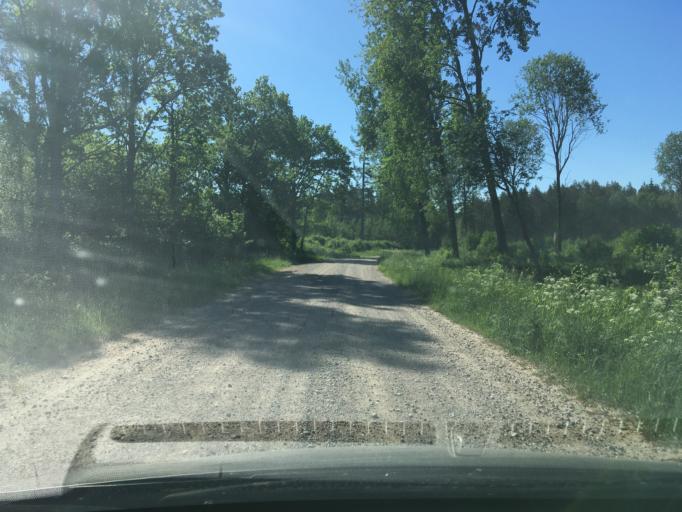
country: EE
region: Laeaene
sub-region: Lihula vald
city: Lihula
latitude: 58.6418
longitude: 23.7889
